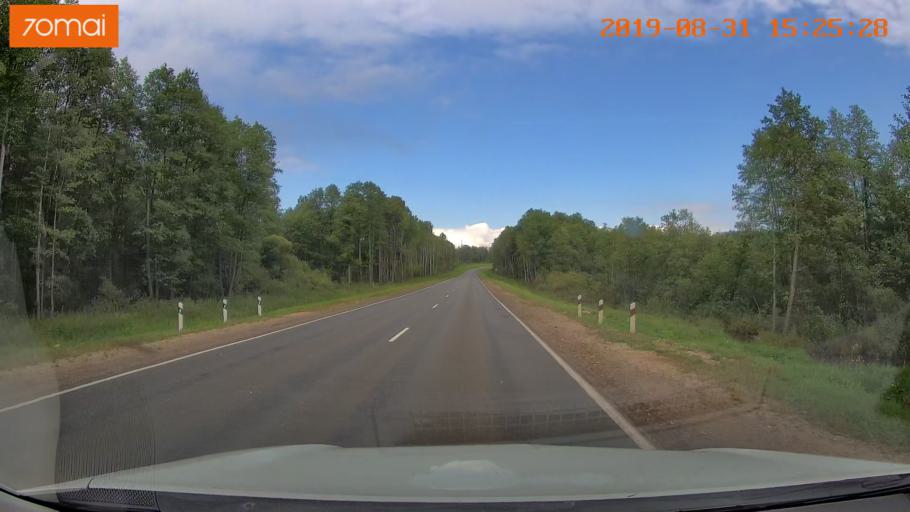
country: RU
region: Kaluga
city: Baryatino
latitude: 54.5418
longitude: 34.5201
